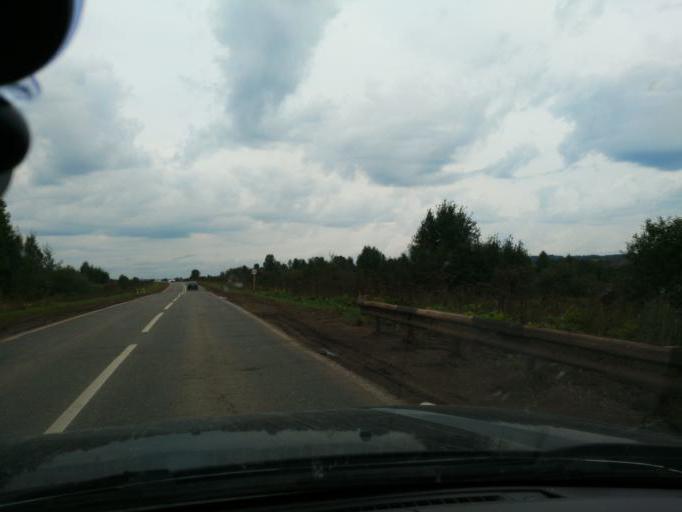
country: RU
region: Perm
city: Chernushka
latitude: 56.7234
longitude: 56.1795
